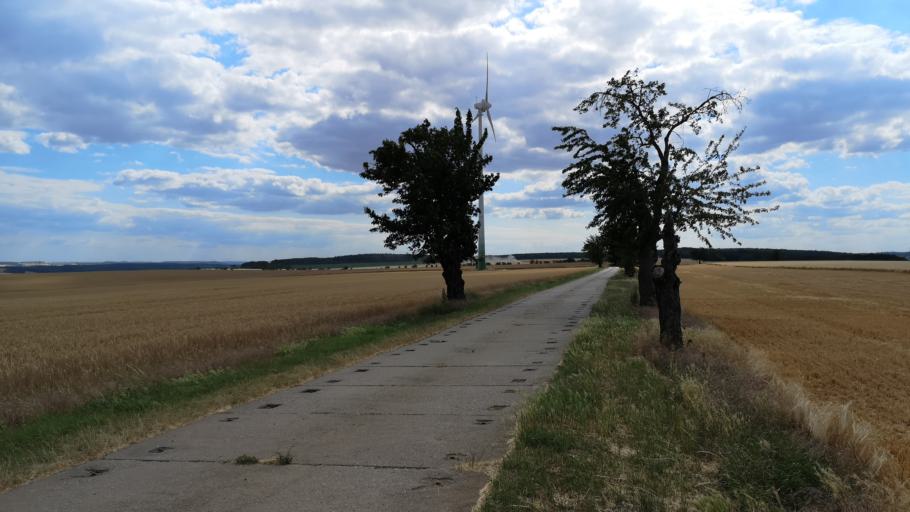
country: DE
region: Saxony-Anhalt
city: Goseck
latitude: 51.2296
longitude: 11.8671
